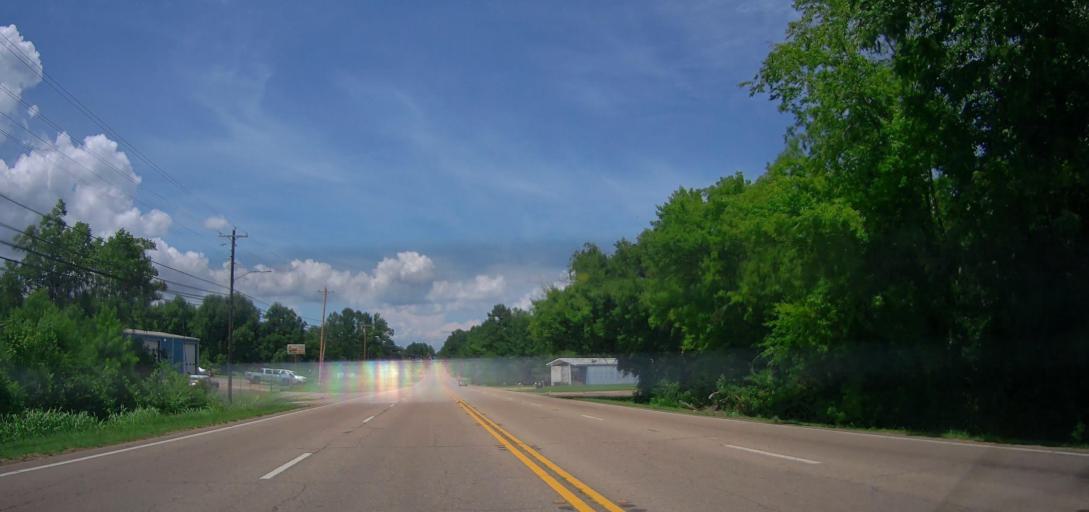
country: US
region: Mississippi
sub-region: Lee County
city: Verona
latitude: 34.1840
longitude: -88.7199
